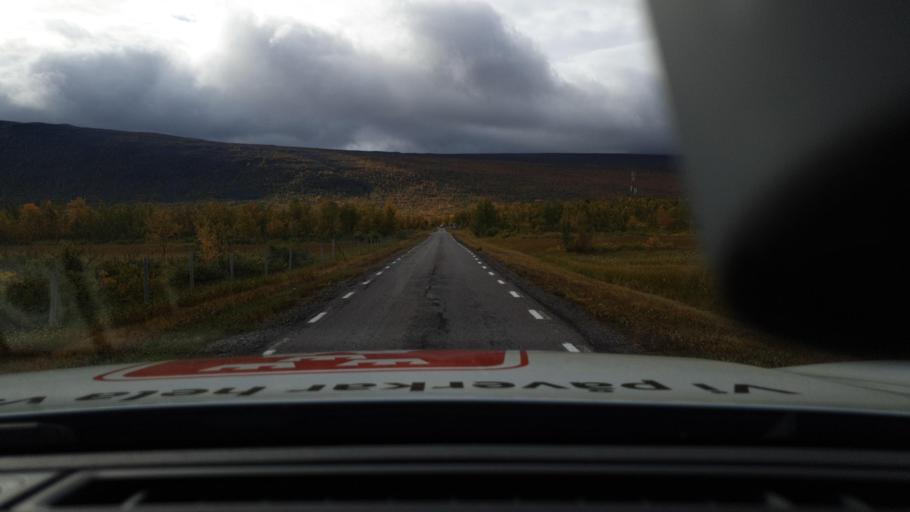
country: SE
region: Norrbotten
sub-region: Kiruna Kommun
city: Kiruna
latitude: 67.8547
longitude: 19.0206
